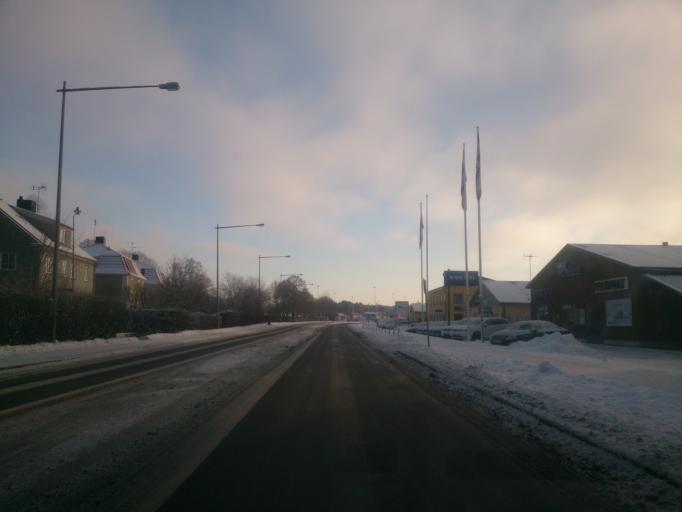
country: SE
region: OEstergoetland
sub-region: Soderkopings Kommun
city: Soederkoeping
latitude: 58.4777
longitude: 16.3304
